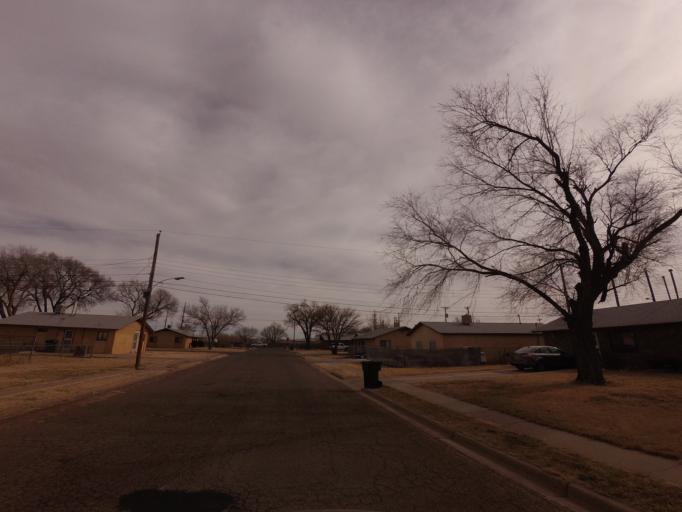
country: US
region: New Mexico
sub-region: Curry County
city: Clovis
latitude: 34.4057
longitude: -103.2329
